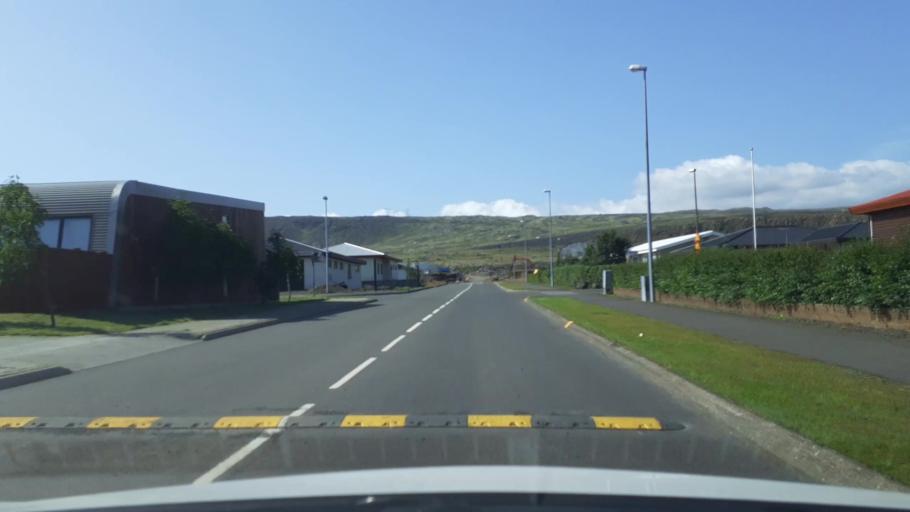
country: IS
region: South
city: Hveragerdi
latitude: 63.9999
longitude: -21.2038
